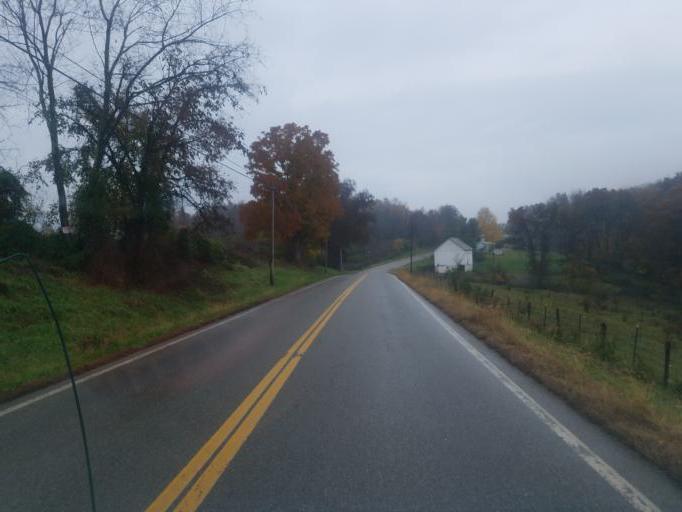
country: US
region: Ohio
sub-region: Morgan County
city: McConnelsville
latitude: 39.5194
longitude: -81.8506
